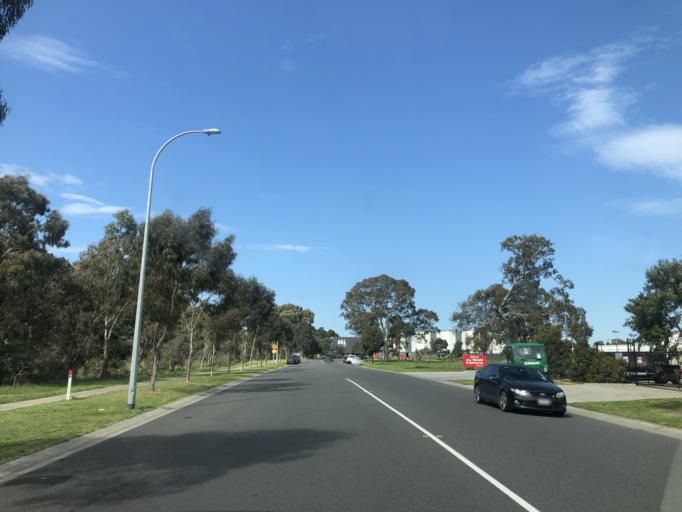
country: AU
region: Victoria
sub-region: Casey
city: Hampton Park
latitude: -38.0416
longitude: 145.2374
